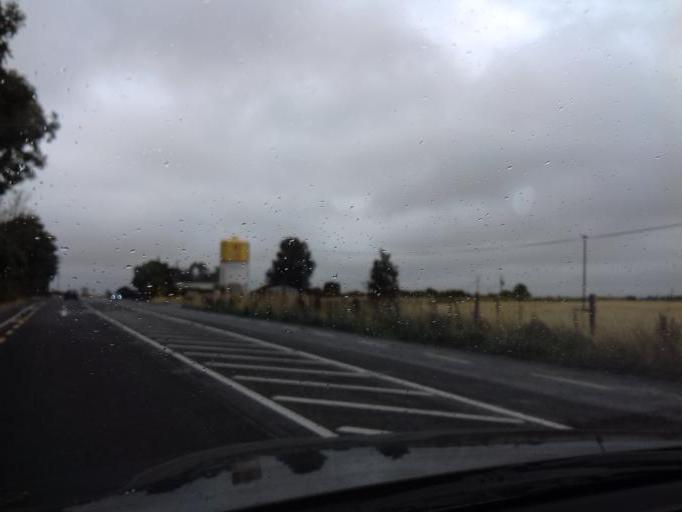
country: IE
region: Leinster
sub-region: County Carlow
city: Bagenalstown
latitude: 52.7581
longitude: -6.9571
